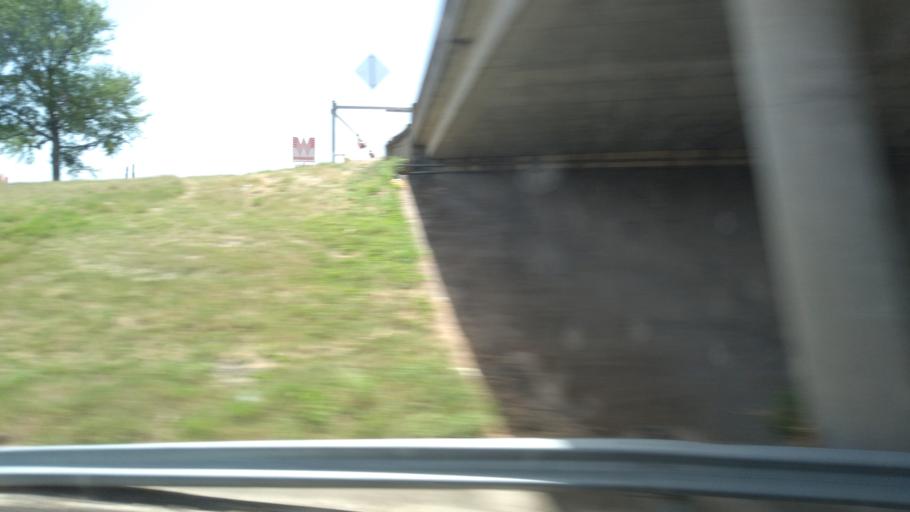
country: US
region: Texas
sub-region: McLennan County
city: Woodway
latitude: 31.5126
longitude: -97.1883
